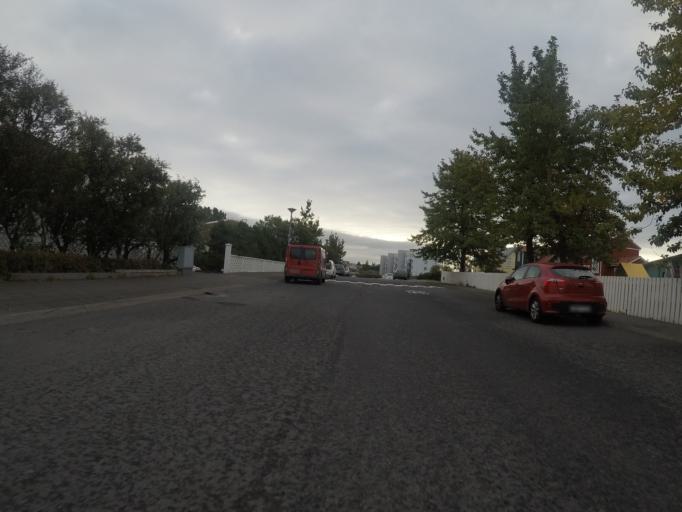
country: IS
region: Capital Region
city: Seltjarnarnes
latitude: 64.1356
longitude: -21.9597
